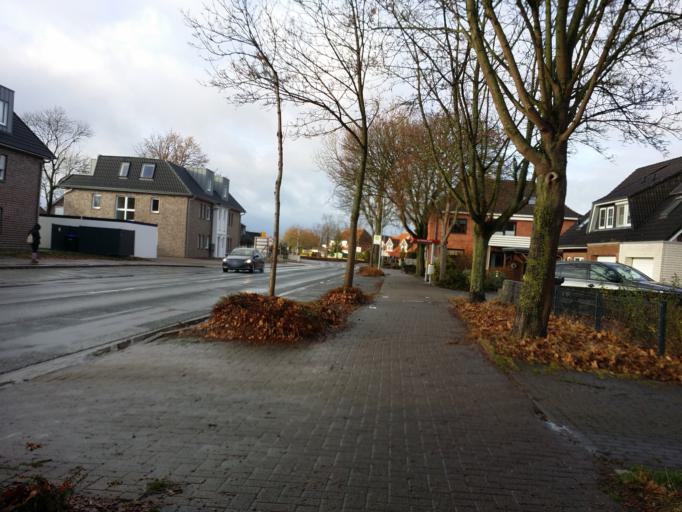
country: DE
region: Lower Saxony
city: Stuhr
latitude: 52.9905
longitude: 8.8084
